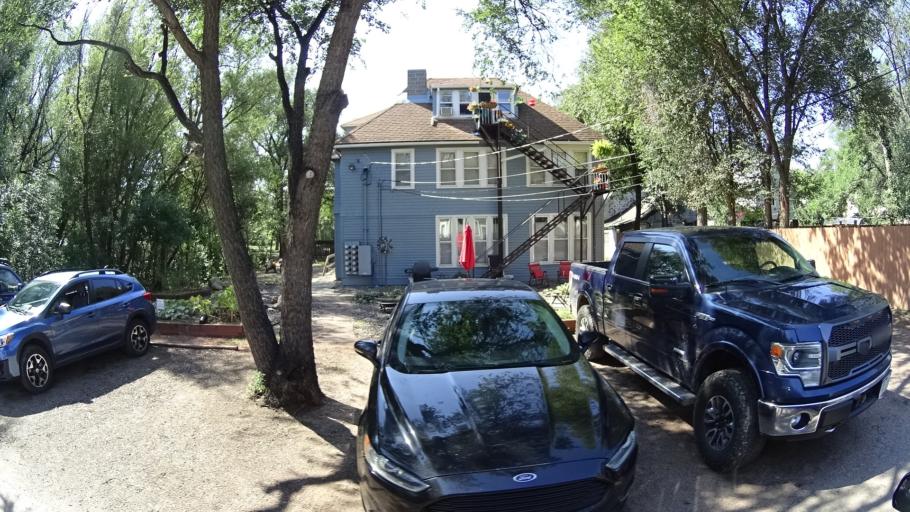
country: US
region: Colorado
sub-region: El Paso County
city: Colorado Springs
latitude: 38.8427
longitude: -104.8130
